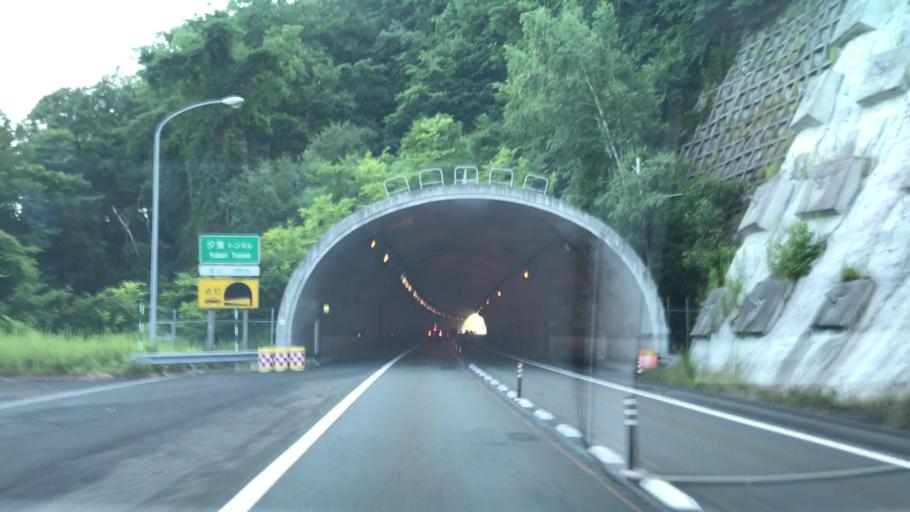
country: JP
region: Hokkaido
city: Chitose
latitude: 42.9084
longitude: 142.0126
